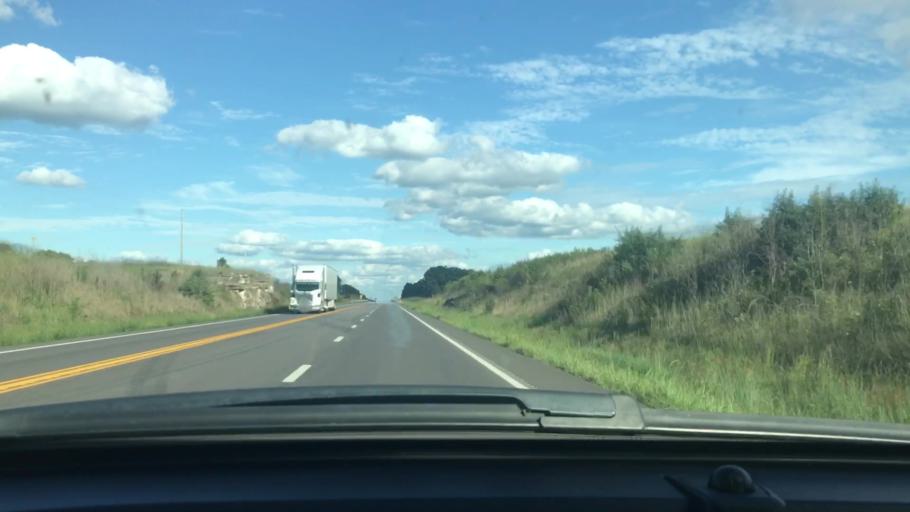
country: US
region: Missouri
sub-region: Oregon County
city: Thayer
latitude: 36.5851
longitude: -91.6203
